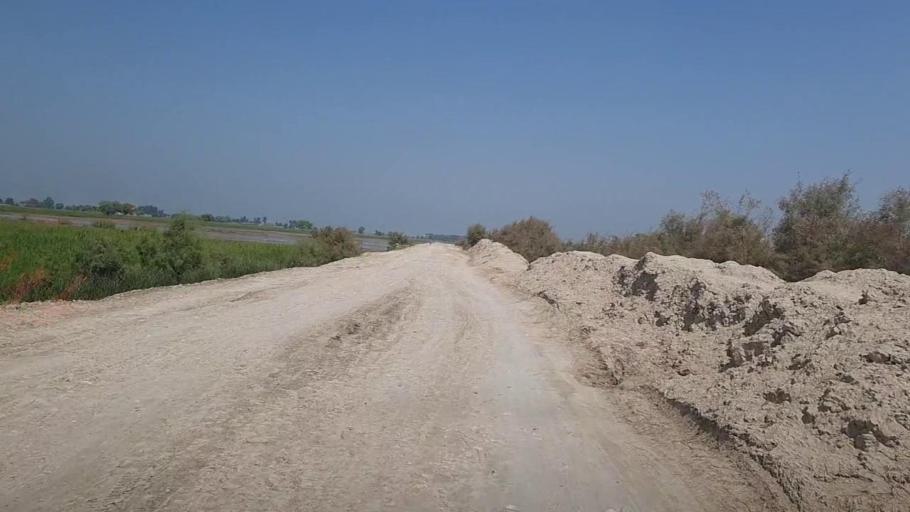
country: PK
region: Sindh
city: Kandhkot
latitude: 28.2974
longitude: 69.2916
